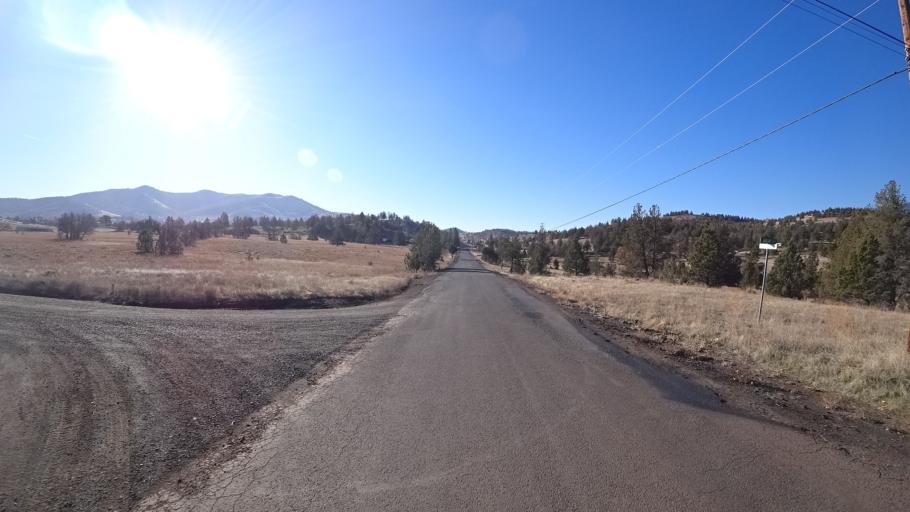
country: US
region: California
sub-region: Siskiyou County
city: Montague
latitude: 41.8906
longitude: -122.4263
